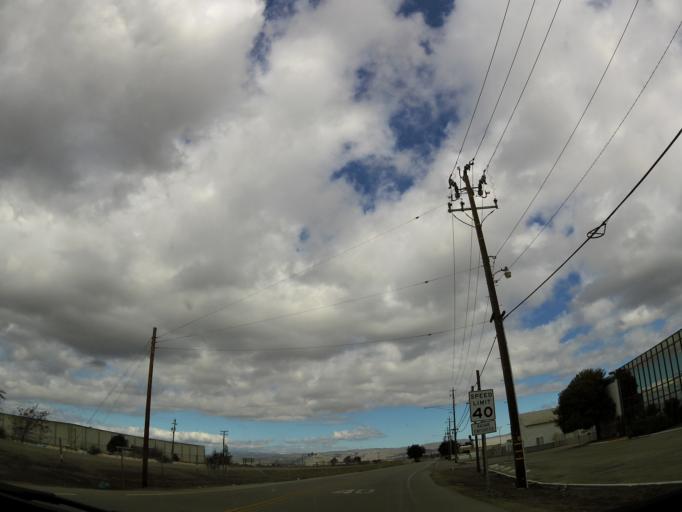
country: US
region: California
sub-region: San Benito County
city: Hollister
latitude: 36.8696
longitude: -121.4007
